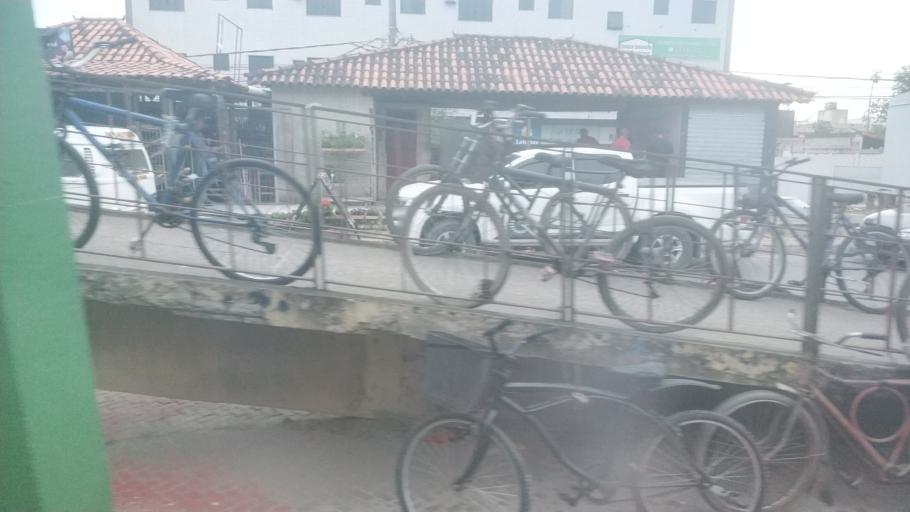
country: BR
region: Rio de Janeiro
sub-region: Seropedica
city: Seropedica
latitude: -22.7470
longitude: -43.6997
